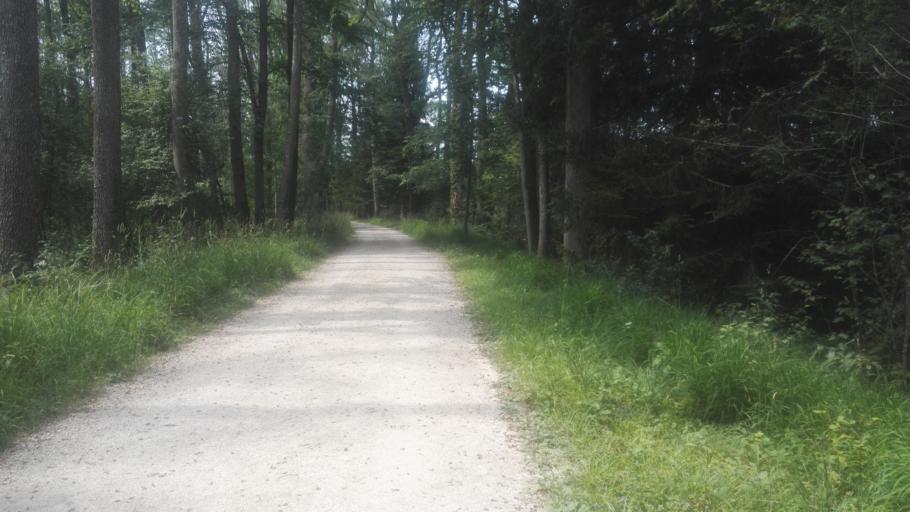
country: DE
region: Bavaria
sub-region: Upper Bavaria
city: Chiemsee
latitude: 47.8636
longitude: 12.4046
